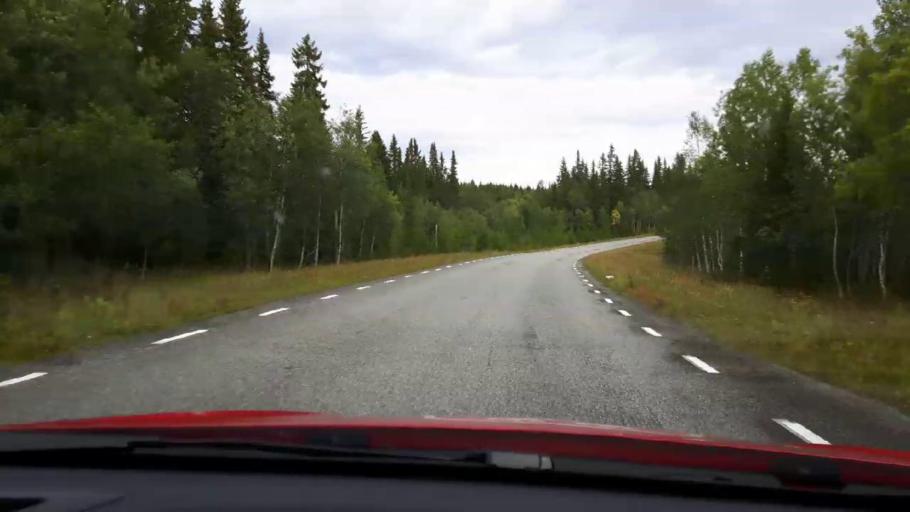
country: SE
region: Jaemtland
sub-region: Are Kommun
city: Are
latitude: 63.7132
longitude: 12.9593
